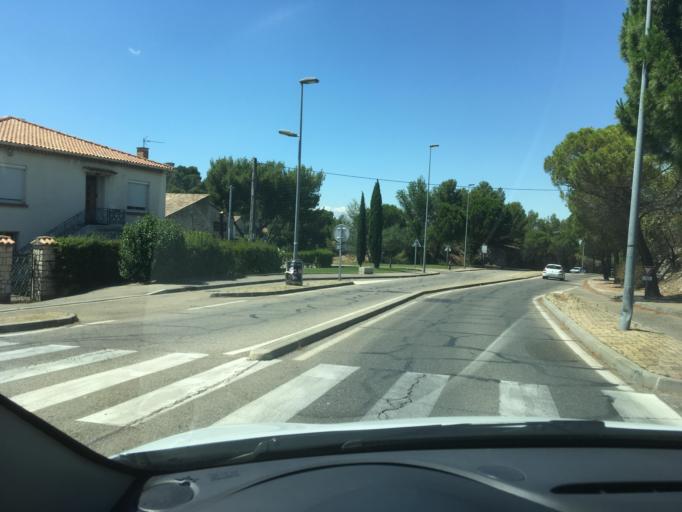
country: FR
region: Provence-Alpes-Cote d'Azur
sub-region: Departement des Bouches-du-Rhone
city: Chateaurenard
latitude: 43.8801
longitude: 4.8629
